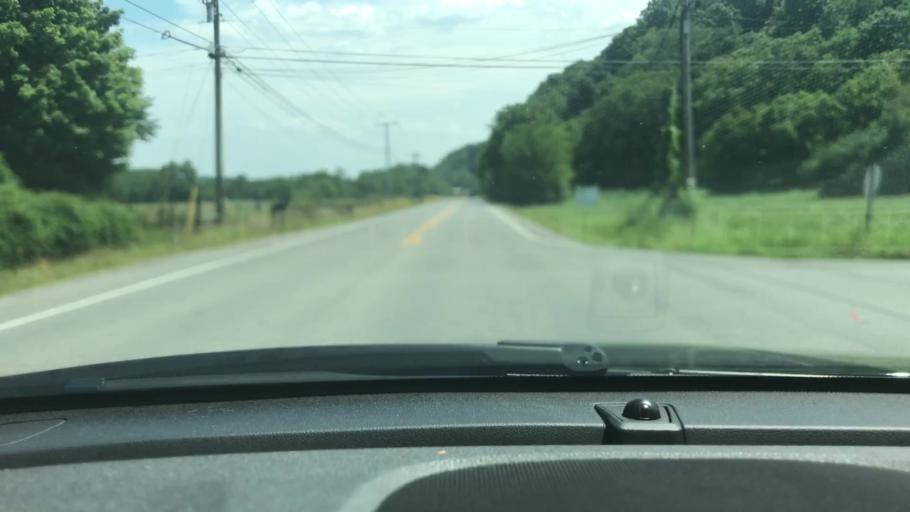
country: US
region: Tennessee
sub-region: Sumner County
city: Shackle Island
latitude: 36.4017
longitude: -86.6310
